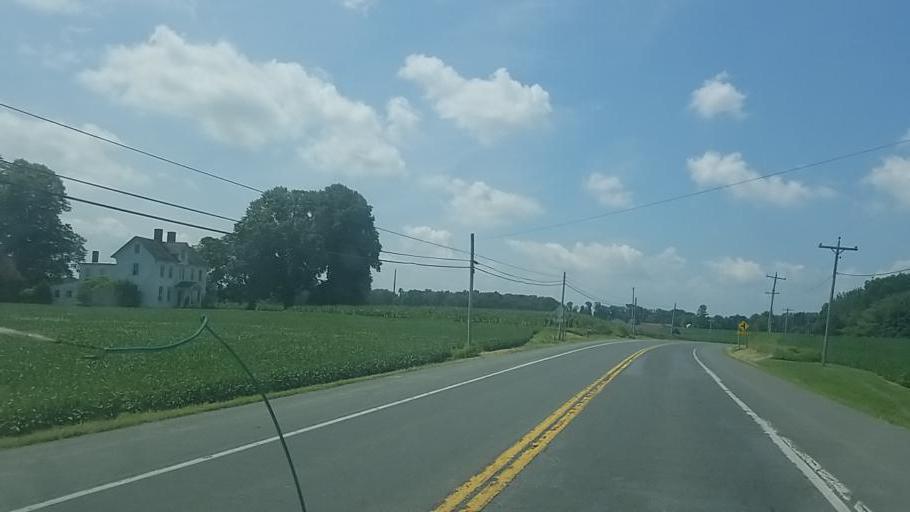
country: US
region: Maryland
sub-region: Talbot County
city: Easton
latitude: 38.7738
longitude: -76.0239
